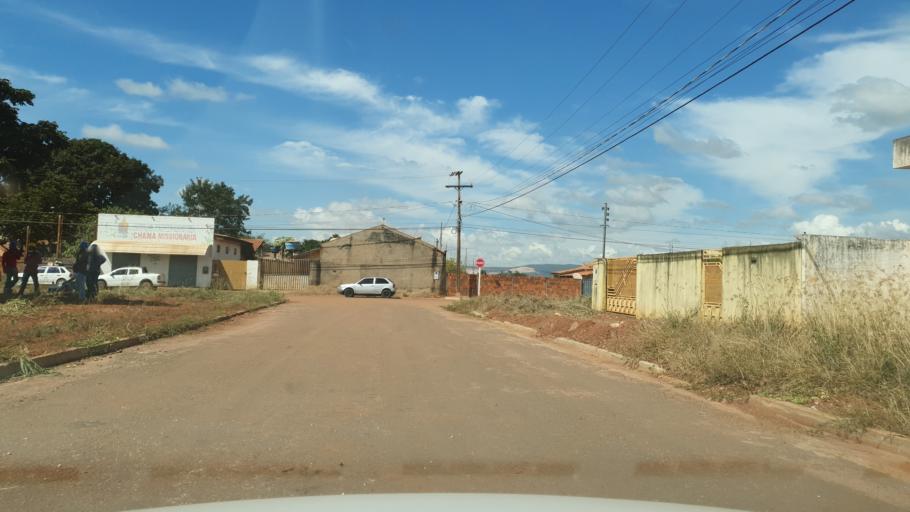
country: BR
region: Mato Grosso
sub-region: Pontes E Lacerda
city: Pontes e Lacerda
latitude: -15.2482
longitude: -59.3134
